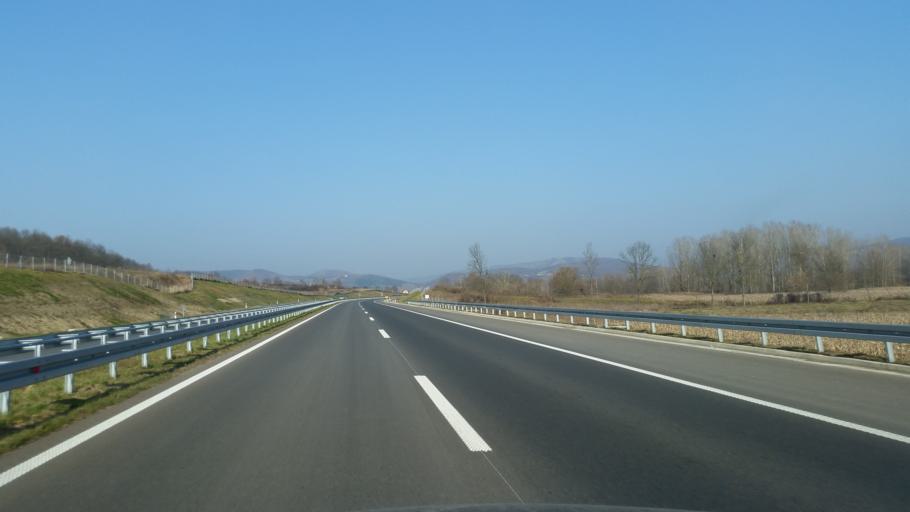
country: RS
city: Prislonica
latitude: 43.9408
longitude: 20.4004
